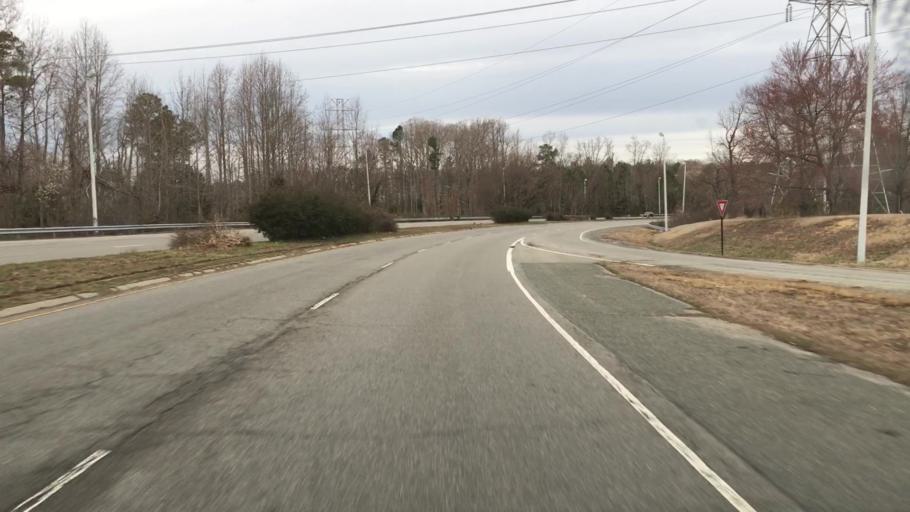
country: US
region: Virginia
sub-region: Chesterfield County
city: Bon Air
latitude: 37.5516
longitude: -77.5697
